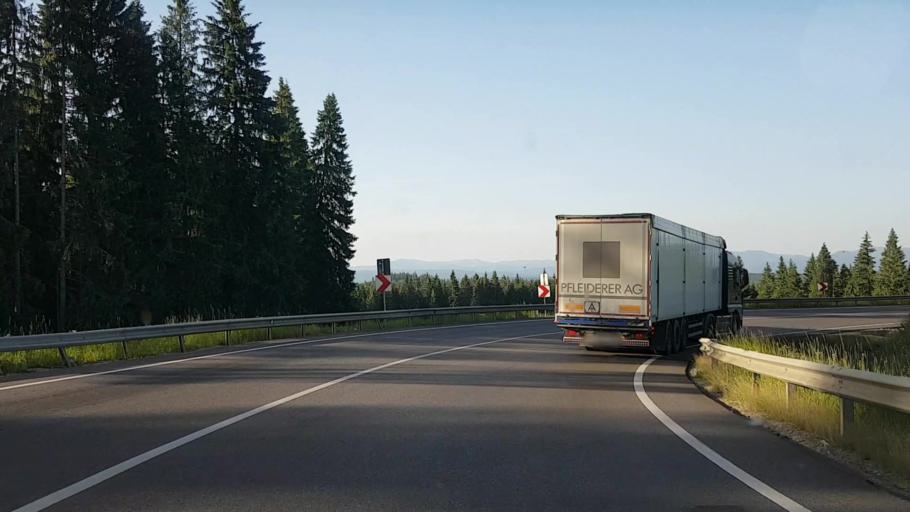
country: RO
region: Suceava
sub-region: Comuna Poiana Stampei
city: Poiana Stampei
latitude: 47.2867
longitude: 25.0622
